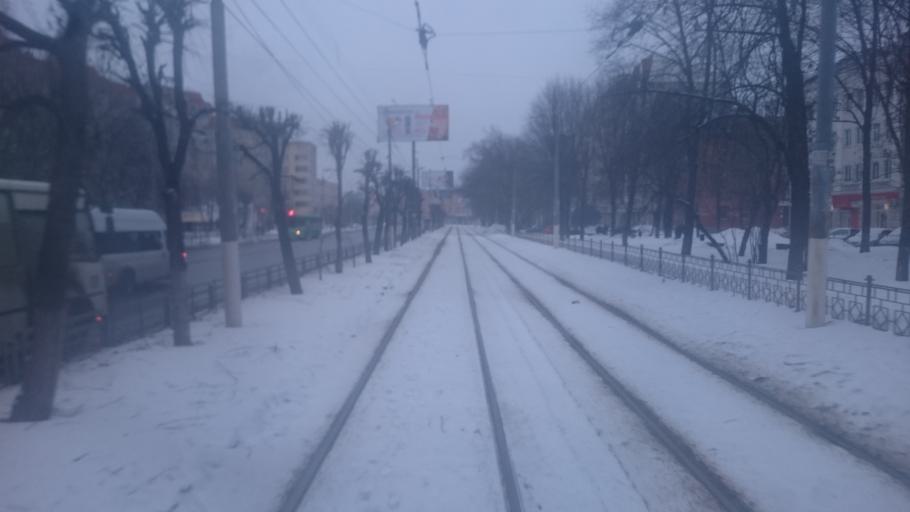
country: RU
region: Tverskaya
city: Tver
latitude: 56.8442
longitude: 35.9027
